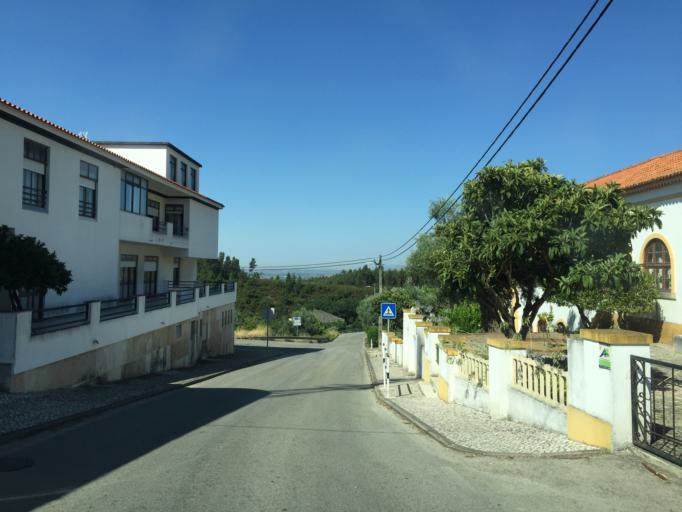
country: PT
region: Santarem
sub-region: Tomar
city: Tomar
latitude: 39.6099
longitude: -8.3335
